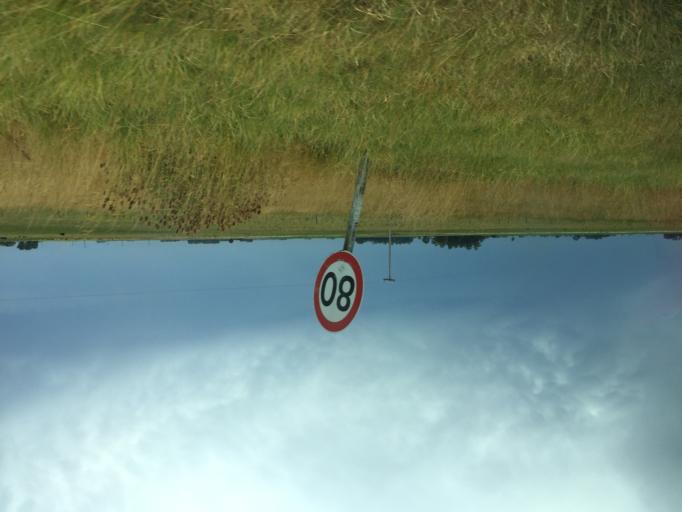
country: AR
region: Buenos Aires
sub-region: Partido de Rauch
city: Rauch
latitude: -36.9212
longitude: -58.9854
